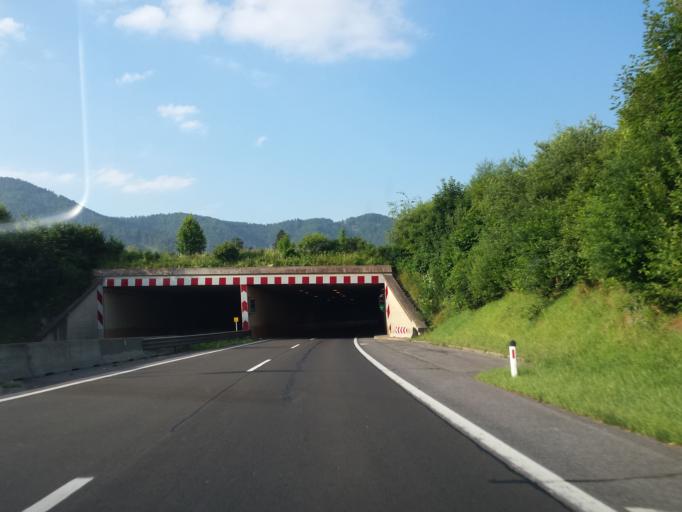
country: AT
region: Styria
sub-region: Politischer Bezirk Bruck-Muerzzuschlag
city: Krieglach
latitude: 47.5451
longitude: 15.5746
